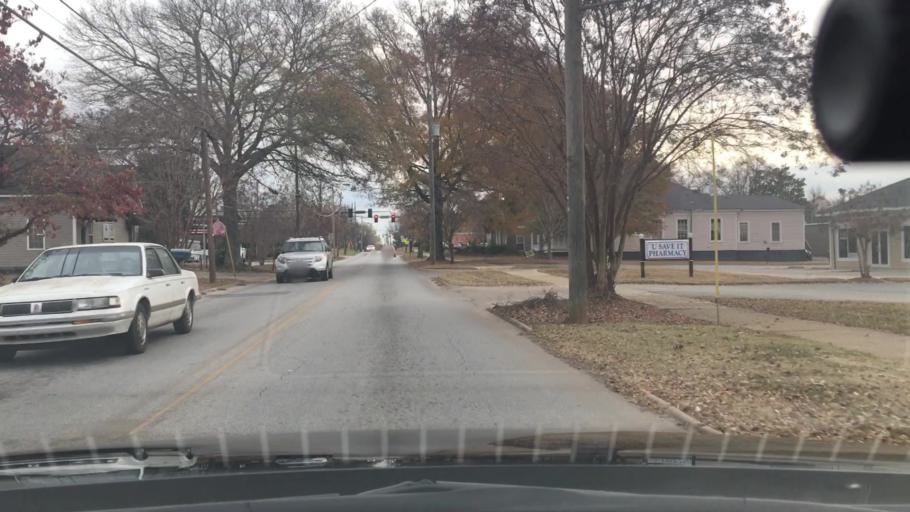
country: US
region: Georgia
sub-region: Spalding County
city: Griffin
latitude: 33.2458
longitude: -84.2671
